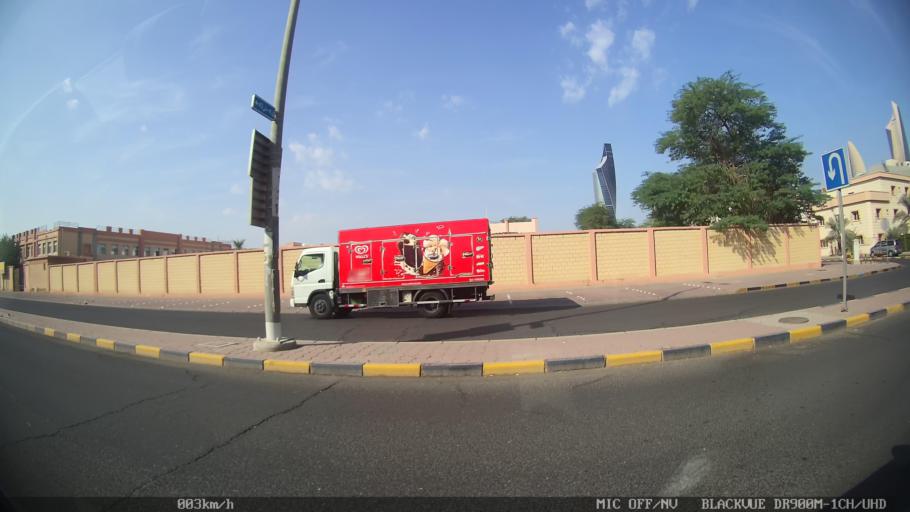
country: KW
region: Muhafazat Hawalli
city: As Salimiyah
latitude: 29.3683
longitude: 48.0833
